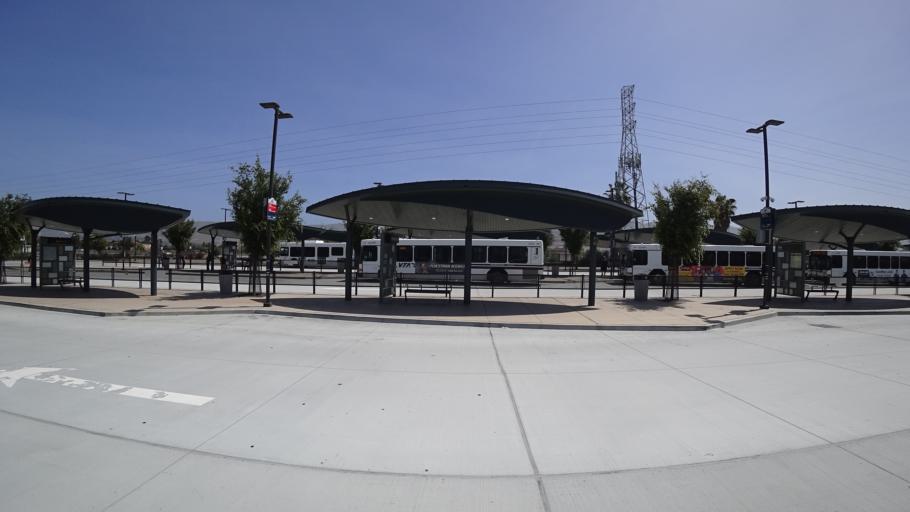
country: US
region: California
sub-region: Santa Clara County
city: Alum Rock
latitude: 37.3274
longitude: -121.8112
